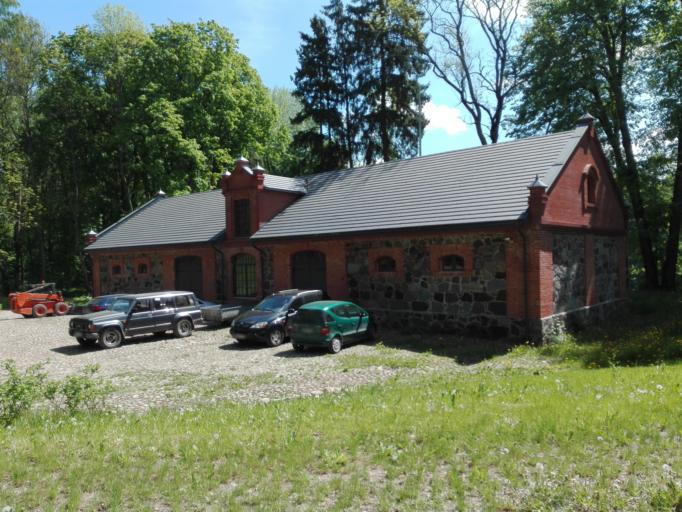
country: LT
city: Trakai
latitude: 54.6618
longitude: 24.9441
